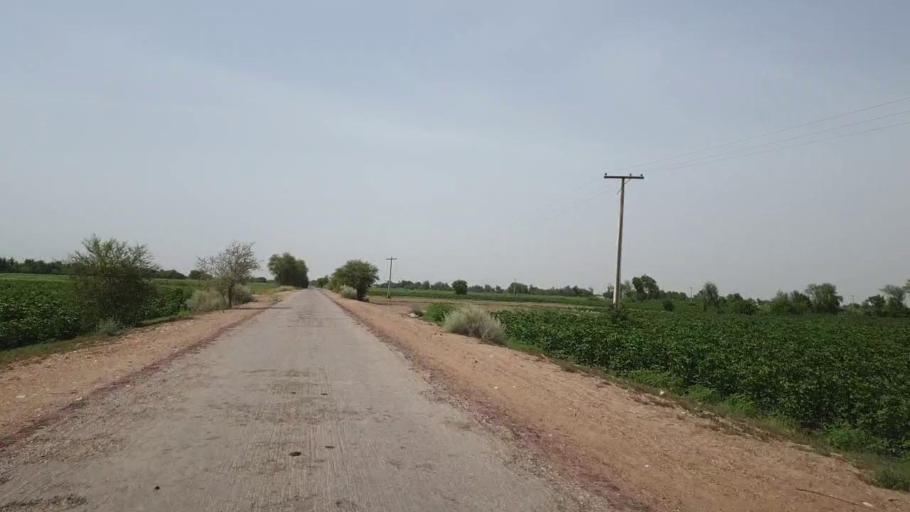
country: PK
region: Sindh
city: Daur
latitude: 26.5287
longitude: 68.4074
